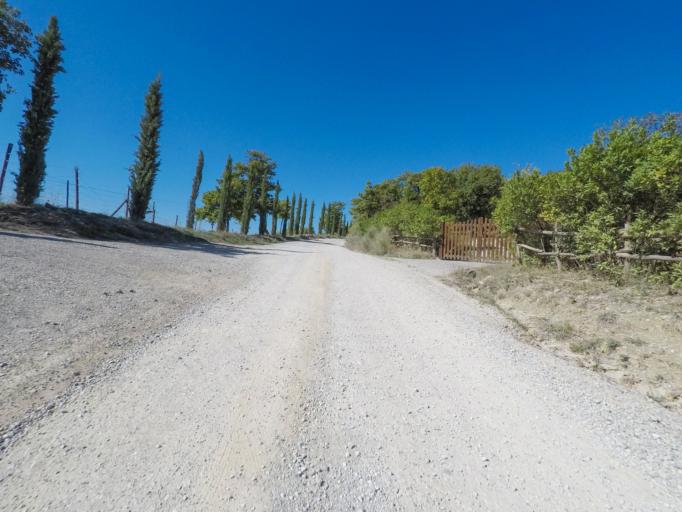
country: IT
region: Tuscany
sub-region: Provincia di Siena
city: Castellina in Chianti
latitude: 43.4358
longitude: 11.3303
